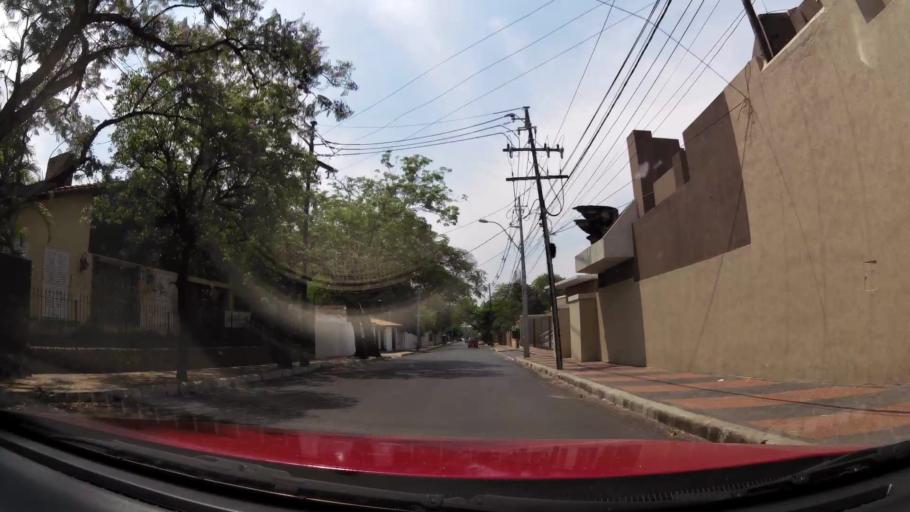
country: PY
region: Asuncion
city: Asuncion
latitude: -25.2909
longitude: -57.5967
